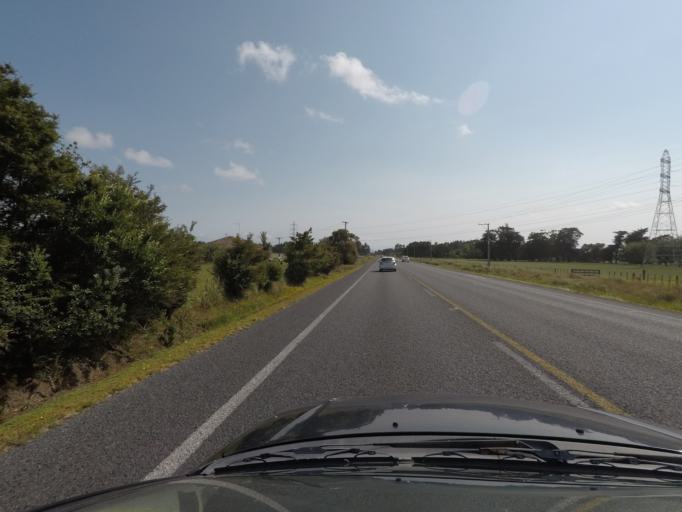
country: NZ
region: Northland
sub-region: Whangarei
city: Ruakaka
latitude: -35.9914
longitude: 174.4233
